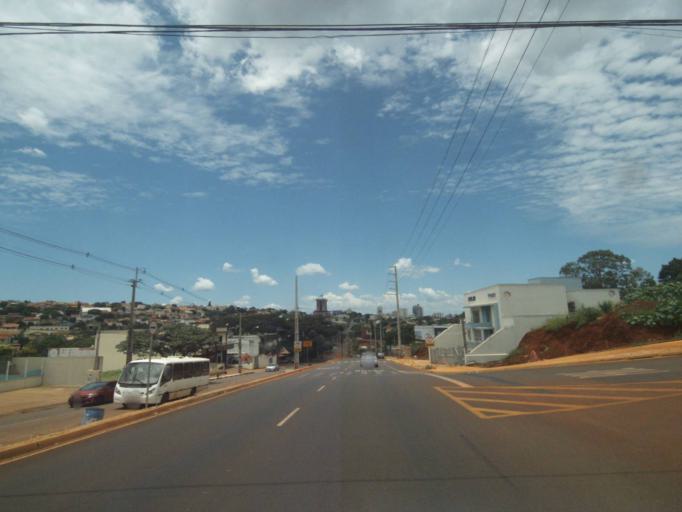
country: BR
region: Parana
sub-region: Londrina
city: Londrina
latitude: -23.3214
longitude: -51.1848
